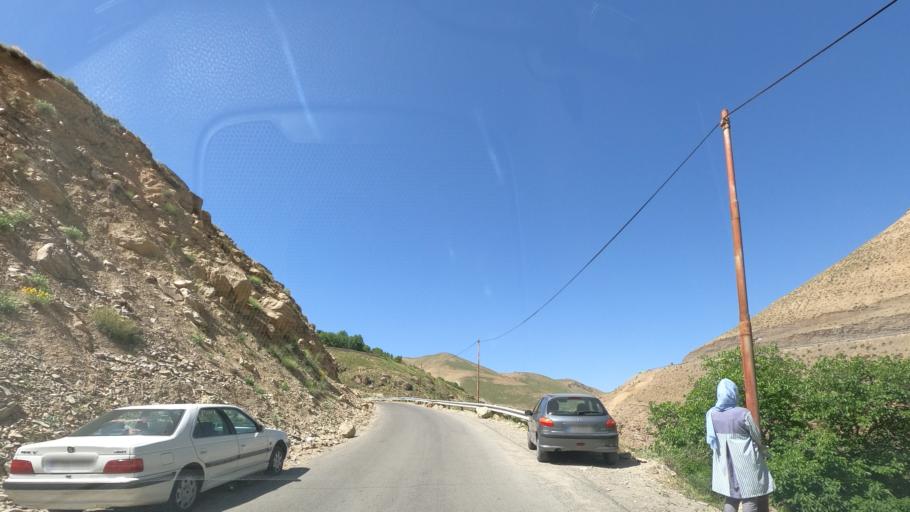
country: IR
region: Alborz
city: Karaj
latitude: 35.9254
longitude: 51.1569
